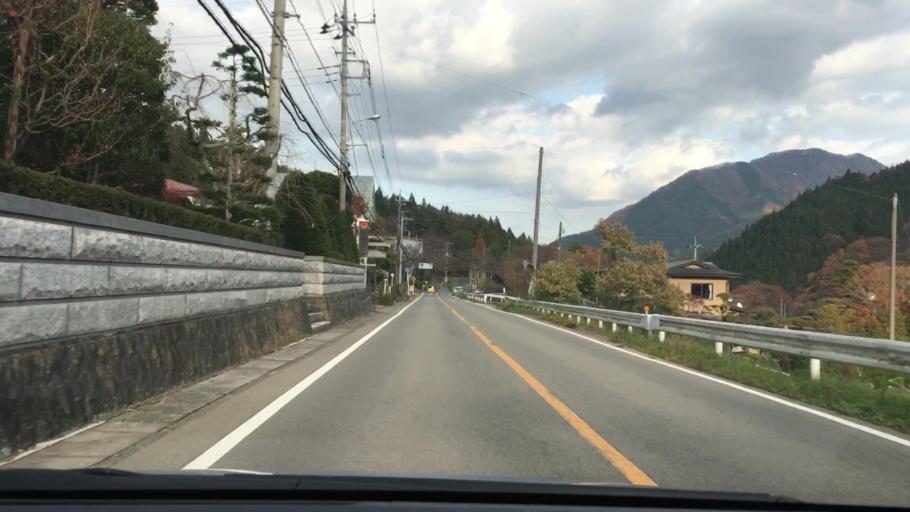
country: JP
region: Yamanashi
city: Otsuki
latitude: 35.4903
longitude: 138.9721
